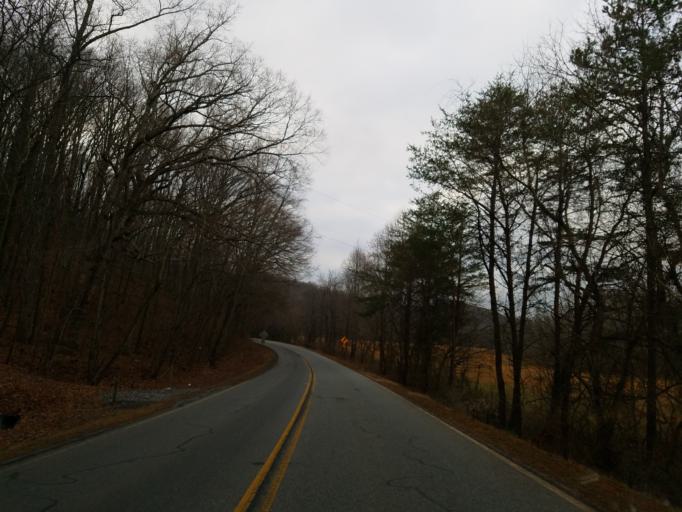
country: US
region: Georgia
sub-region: Bartow County
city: Rydal
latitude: 34.3480
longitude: -84.6666
